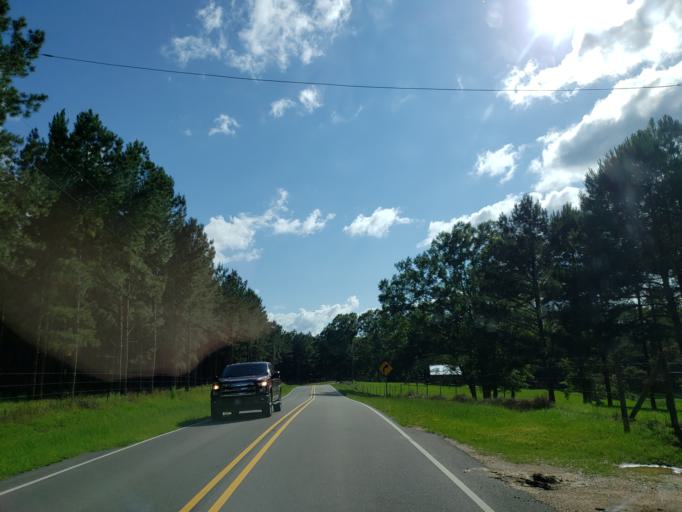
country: US
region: Mississippi
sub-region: Lamar County
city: Sumrall
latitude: 31.3545
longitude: -89.4860
